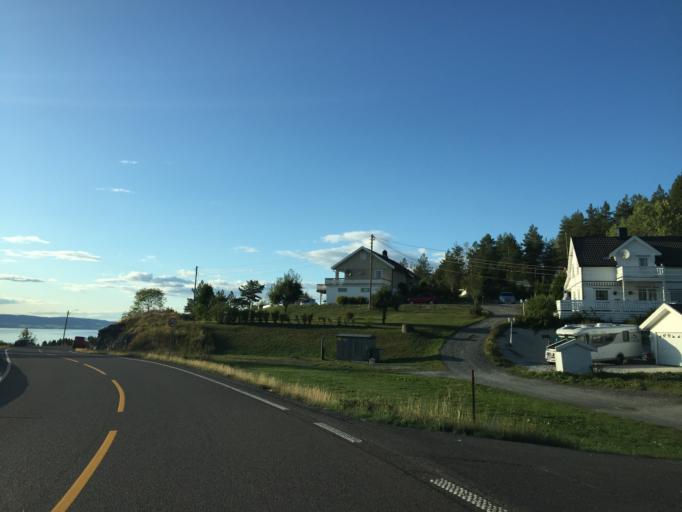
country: NO
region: Akershus
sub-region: Enebakk
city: Flateby
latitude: 59.7982
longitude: 11.2577
